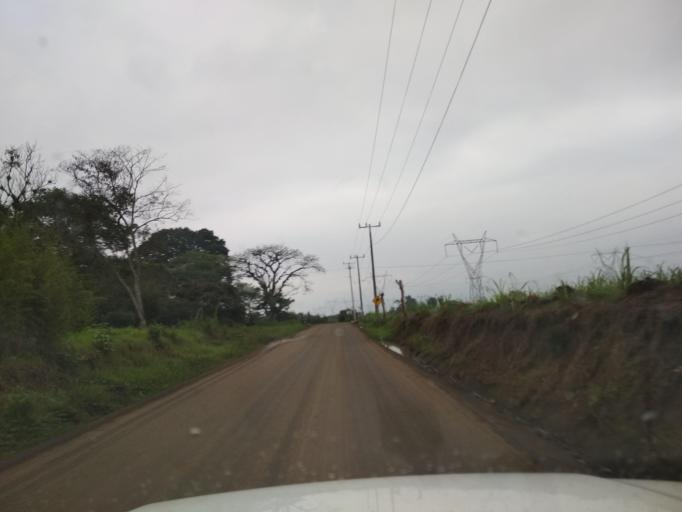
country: MX
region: Veracruz
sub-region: Cordoba
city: Veinte de Noviembre
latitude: 18.8663
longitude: -96.9613
